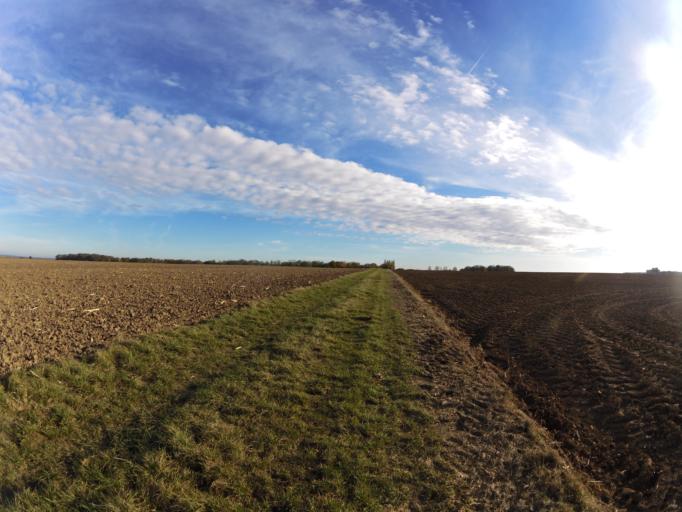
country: DE
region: Bavaria
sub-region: Regierungsbezirk Unterfranken
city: Giebelstadt
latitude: 49.6622
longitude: 9.9631
